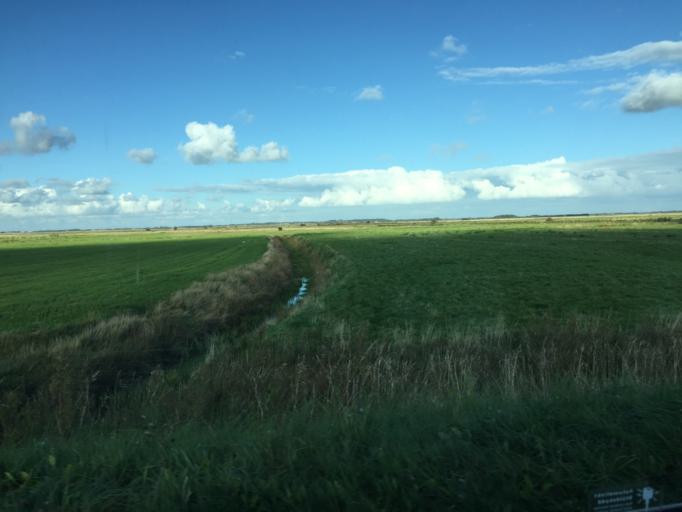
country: DE
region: Schleswig-Holstein
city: Neukirchen
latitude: 54.9113
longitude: 8.7448
